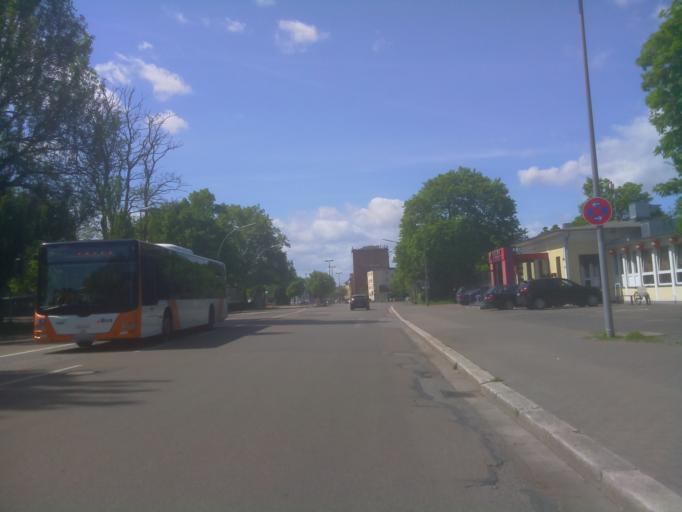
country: DE
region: Rheinland-Pfalz
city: Ludwigshafen am Rhein
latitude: 49.4660
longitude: 8.4391
